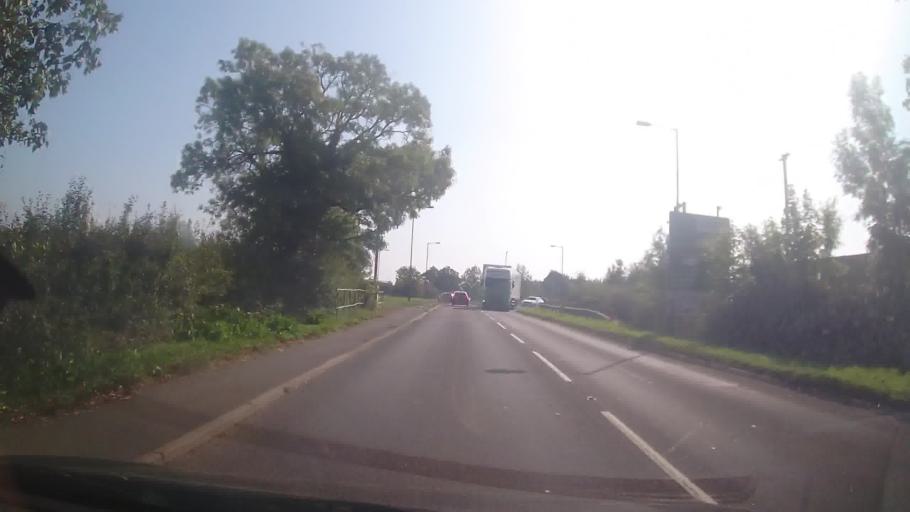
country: GB
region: England
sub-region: Worcestershire
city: Pershore
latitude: 52.1317
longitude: -2.0666
